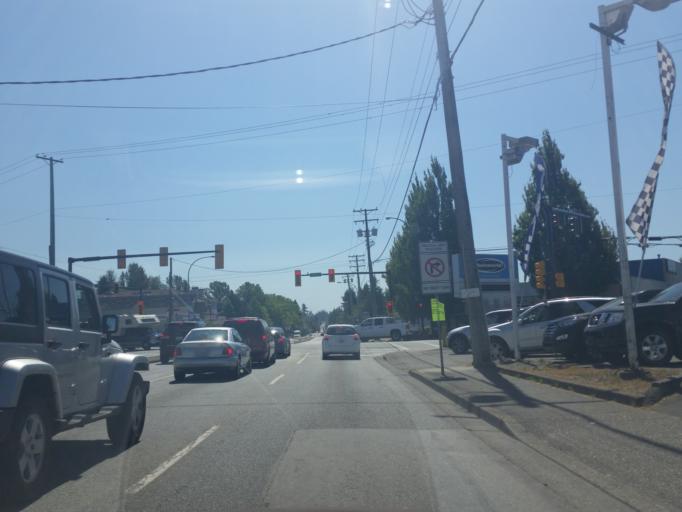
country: CA
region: British Columbia
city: Langley
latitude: 49.1094
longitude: -122.6688
